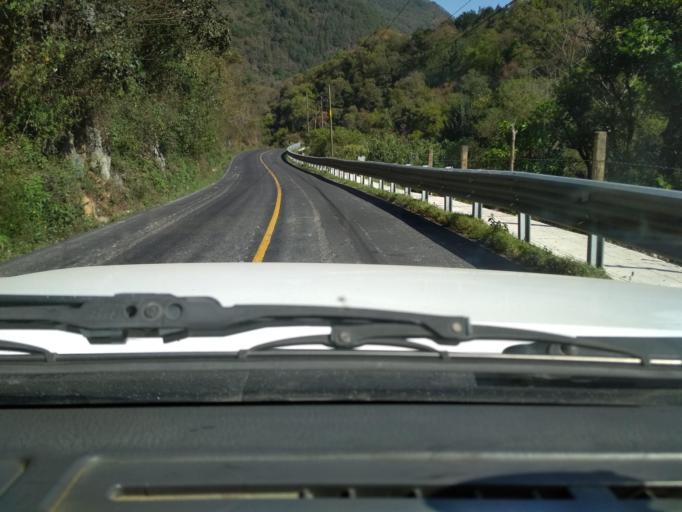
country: MX
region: Veracruz
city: Tequila
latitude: 18.7476
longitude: -97.0898
